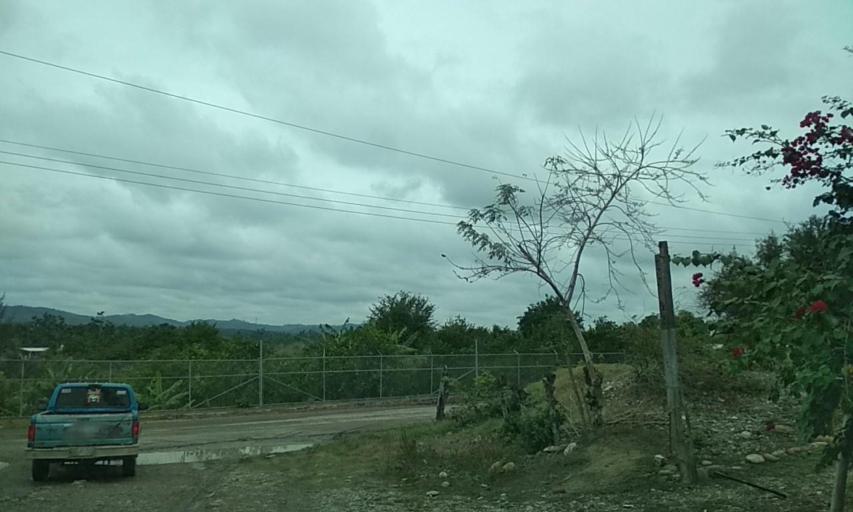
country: MX
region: Puebla
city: Espinal
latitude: 20.3227
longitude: -97.4158
